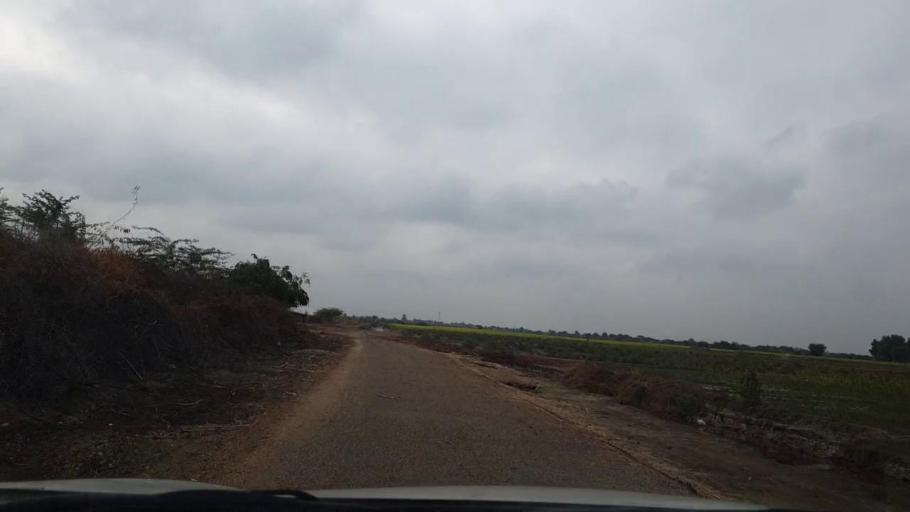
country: PK
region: Sindh
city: Tando Mittha Khan
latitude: 25.8776
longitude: 69.1430
